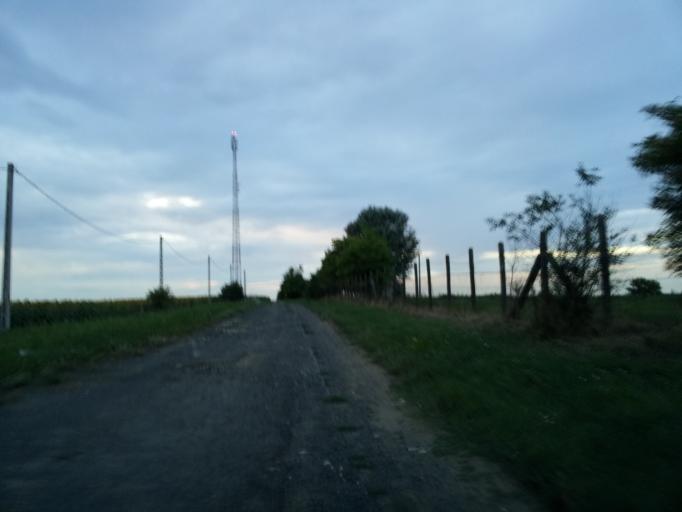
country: HU
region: Somogy
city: Adand
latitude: 46.8502
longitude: 18.1350
